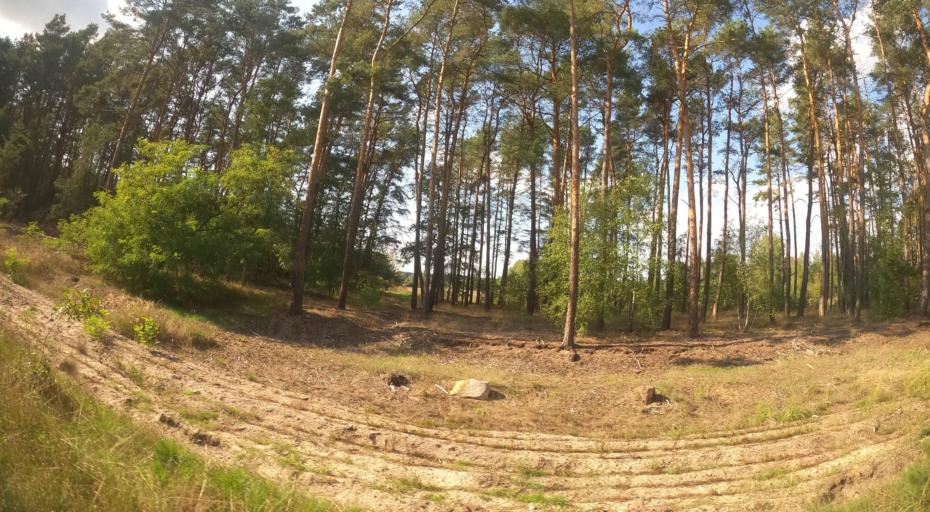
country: PL
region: Lubusz
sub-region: Powiat zielonogorski
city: Swidnica
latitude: 51.8685
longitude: 15.3154
